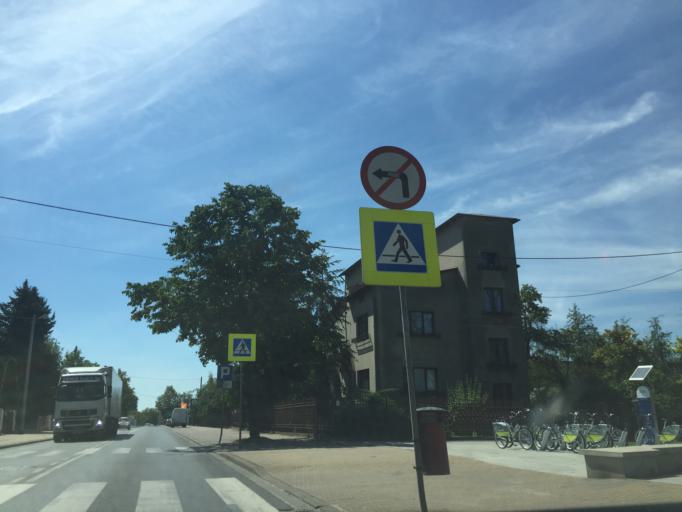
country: PL
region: Lodz Voivodeship
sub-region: Piotrkow Trybunalski
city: Piotrkow Trybunalski
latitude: 51.4084
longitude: 19.7038
